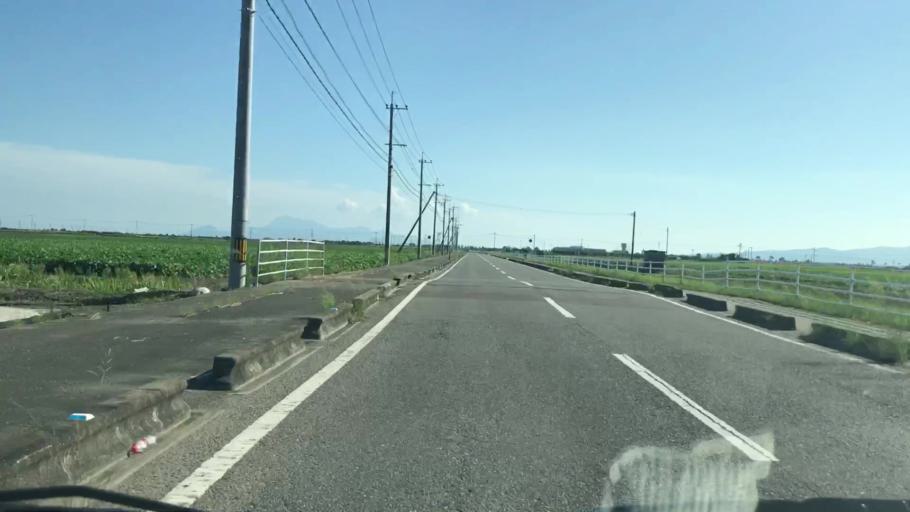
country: JP
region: Saga Prefecture
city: Okawa
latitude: 33.1695
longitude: 130.3101
